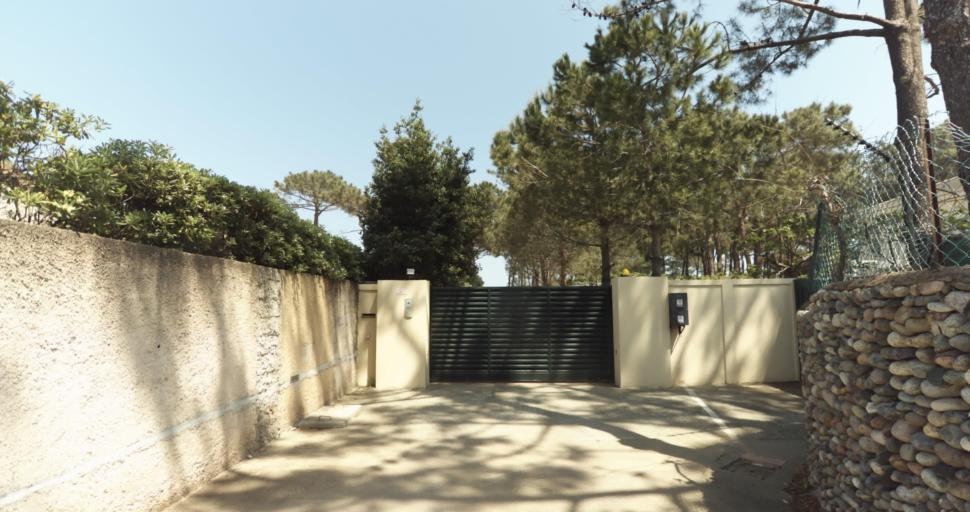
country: FR
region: Corsica
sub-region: Departement de la Haute-Corse
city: Biguglia
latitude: 42.6384
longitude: 9.4612
